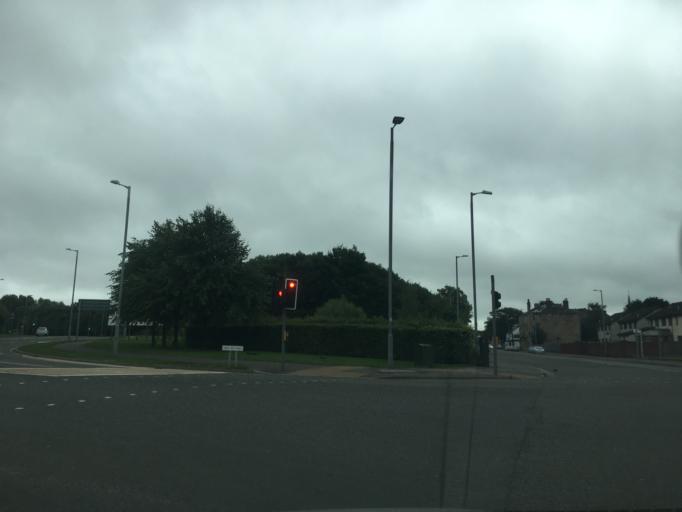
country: GB
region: Scotland
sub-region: Renfrewshire
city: Renfrew
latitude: 55.8839
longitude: -4.3845
